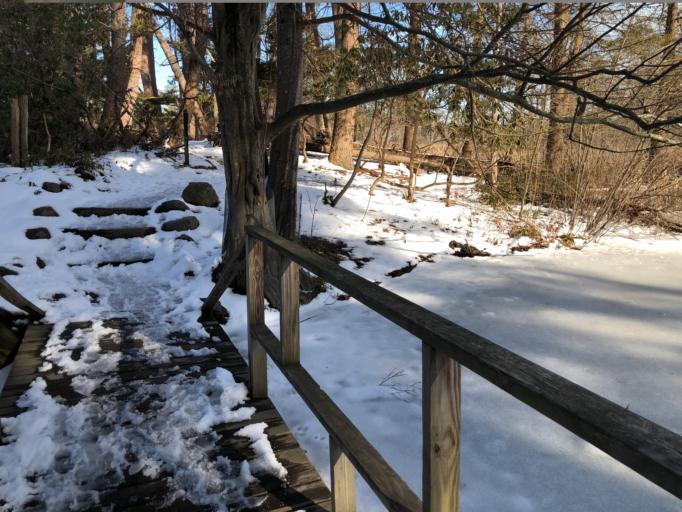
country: US
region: Massachusetts
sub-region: Essex County
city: Topsfield
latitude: 42.6357
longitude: -70.9200
